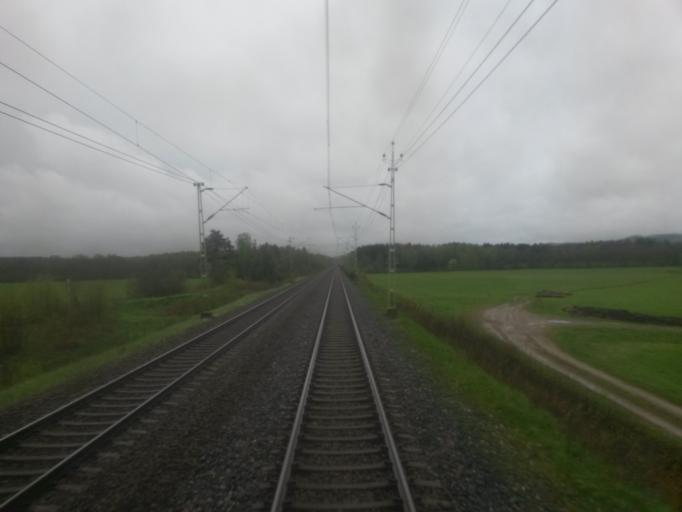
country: SE
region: Vaestra Goetaland
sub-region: Vargarda Kommun
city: Jonstorp
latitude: 57.9809
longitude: 12.6305
